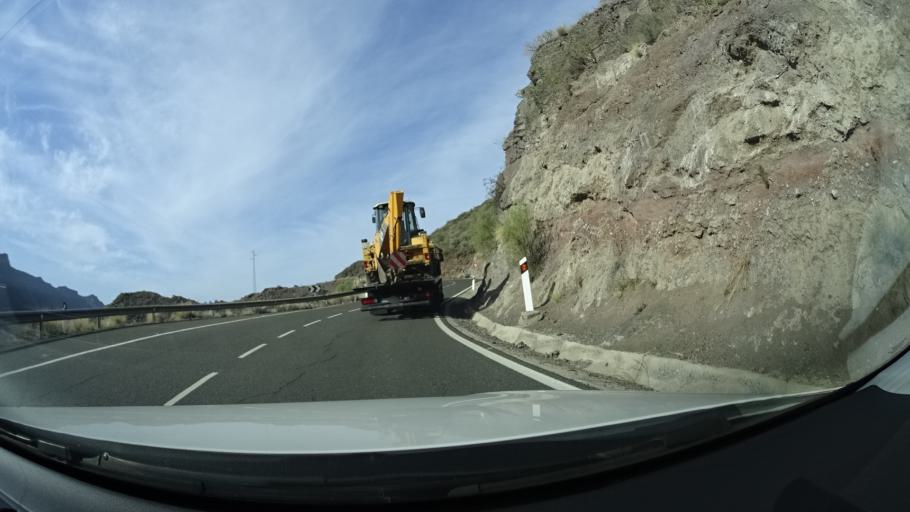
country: ES
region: Canary Islands
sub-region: Provincia de Las Palmas
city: Mogan
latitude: 27.8990
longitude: -15.7154
